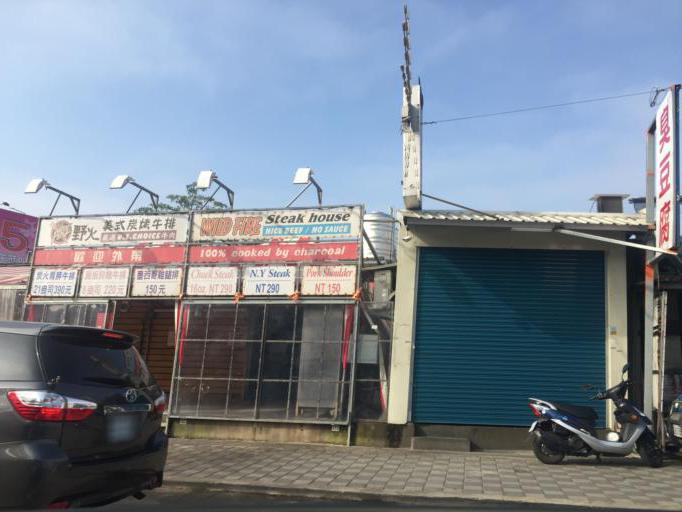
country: TW
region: Taiwan
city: Daxi
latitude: 24.8653
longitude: 121.2224
